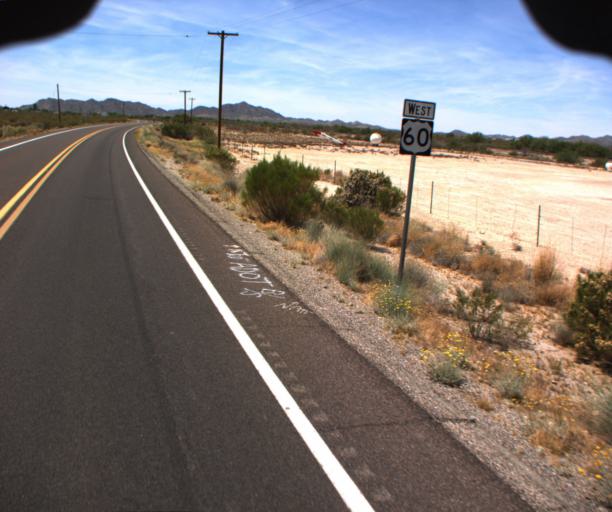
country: US
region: Arizona
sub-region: La Paz County
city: Salome
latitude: 33.7785
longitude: -113.6192
